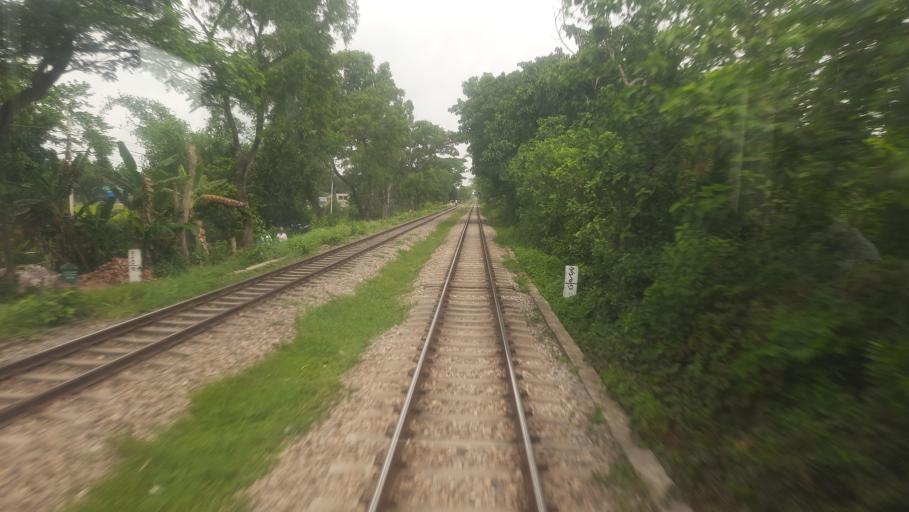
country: BD
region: Dhaka
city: Bhairab Bazar
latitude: 23.9762
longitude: 91.0830
